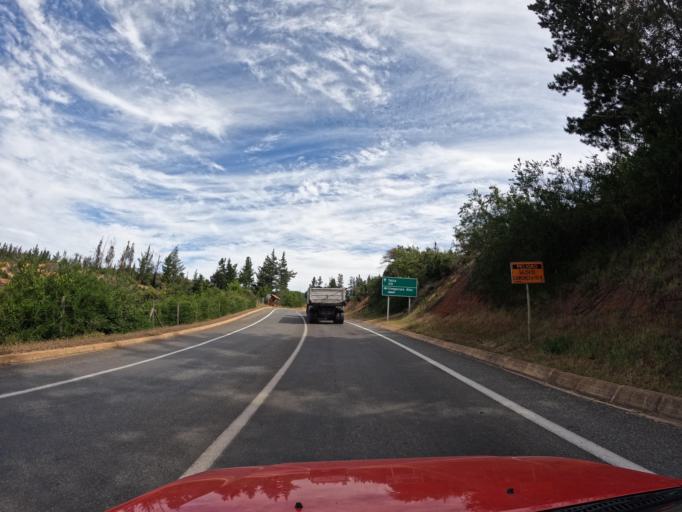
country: CL
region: Maule
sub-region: Provincia de Talca
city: Talca
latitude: -35.1656
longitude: -71.9728
